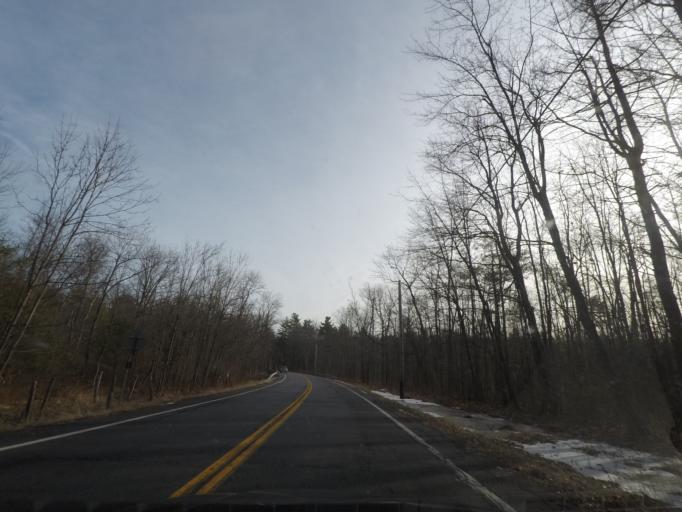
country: US
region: New York
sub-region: Saratoga County
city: Stillwater
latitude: 42.9914
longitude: -73.7119
